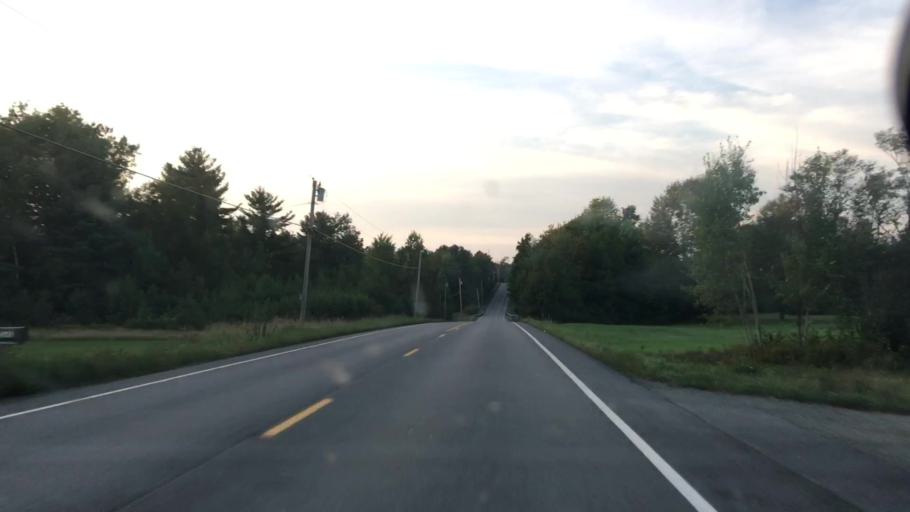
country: US
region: Maine
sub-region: Penobscot County
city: Hermon
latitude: 44.7484
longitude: -68.9686
